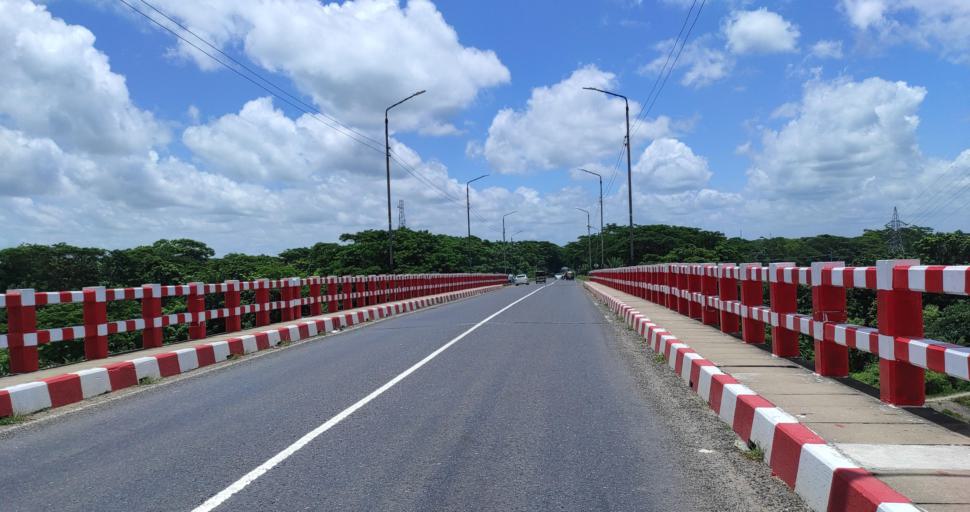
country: BD
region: Barisal
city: Gaurnadi
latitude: 22.8239
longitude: 90.2641
